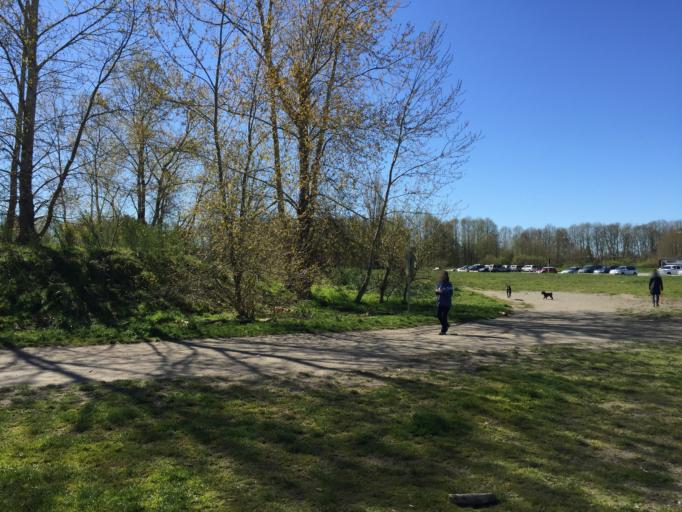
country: CA
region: British Columbia
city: Richmond
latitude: 49.2133
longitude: -123.1678
